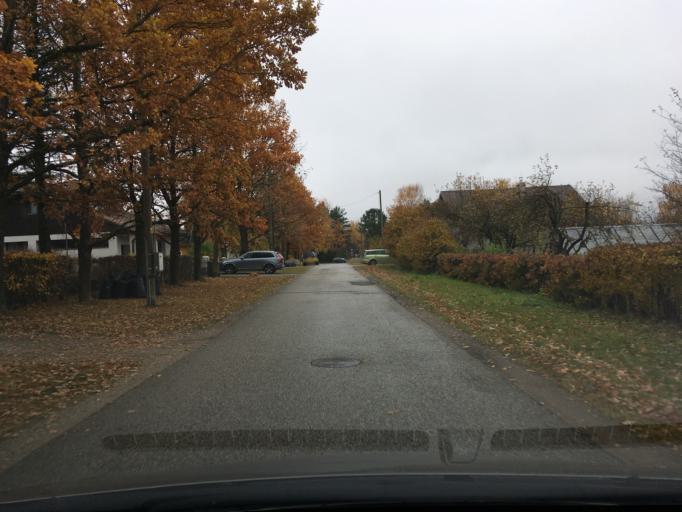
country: EE
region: Tartu
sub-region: UElenurme vald
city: Ulenurme
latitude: 58.3471
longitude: 26.7764
